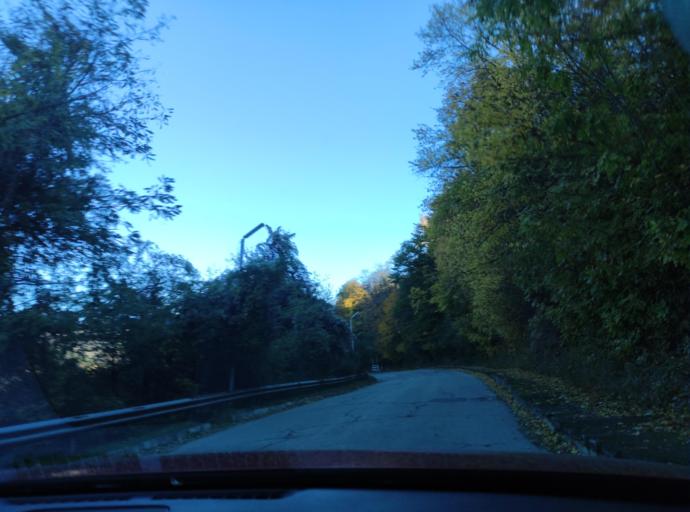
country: BG
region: Montana
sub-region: Obshtina Chiprovtsi
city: Chiprovtsi
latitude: 43.3820
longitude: 22.8948
